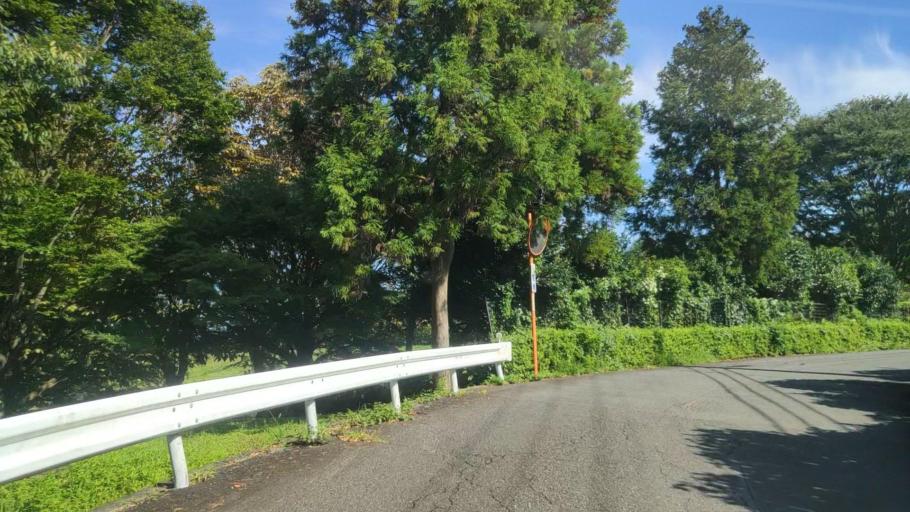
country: JP
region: Shizuoka
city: Shizuoka-shi
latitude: 34.9848
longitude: 138.4759
